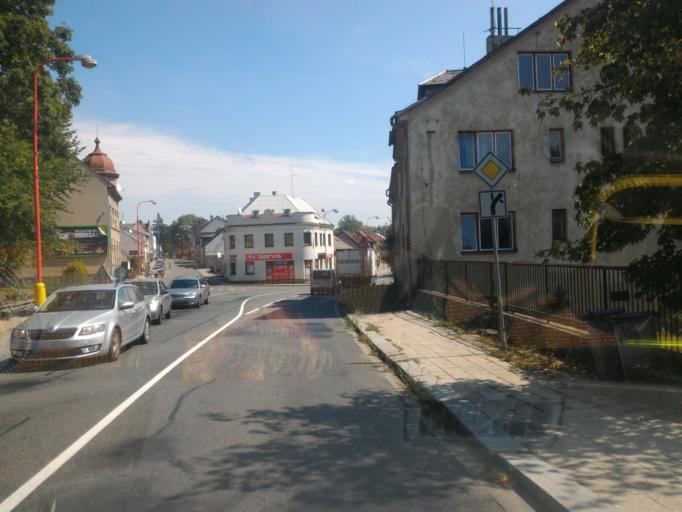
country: CZ
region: Pardubicky
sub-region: Okres Chrudim
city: Hlinsko
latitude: 49.7635
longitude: 15.9034
